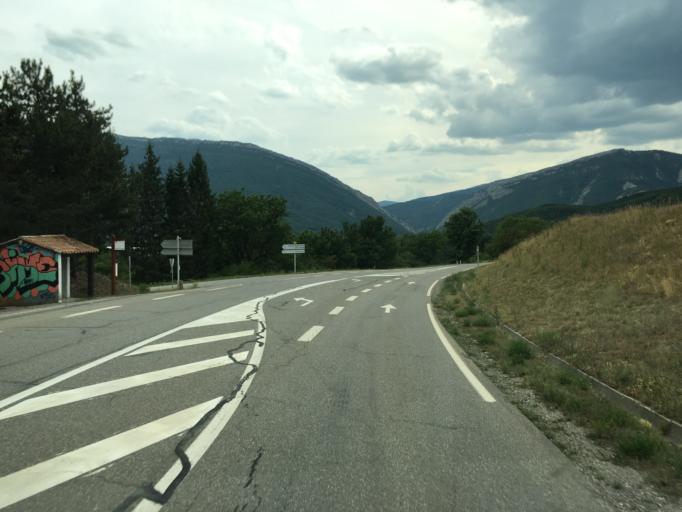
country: FR
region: Provence-Alpes-Cote d'Azur
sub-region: Departement des Hautes-Alpes
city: Serres
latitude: 44.4670
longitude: 5.7513
